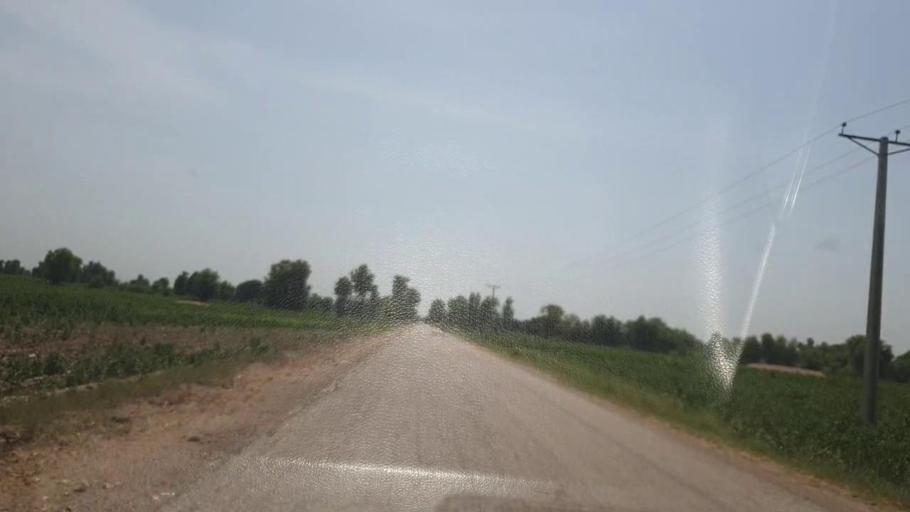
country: PK
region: Sindh
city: Kandiari
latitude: 27.0539
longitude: 68.5547
